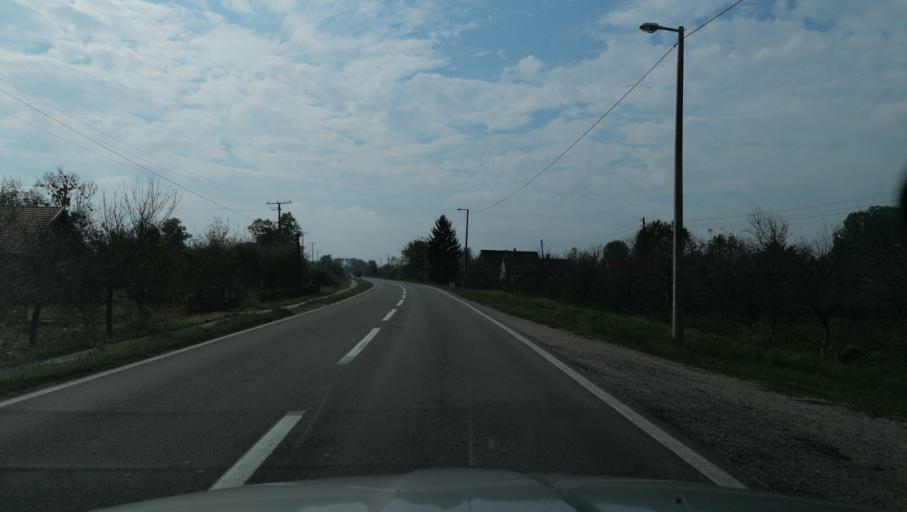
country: BA
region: Republika Srpska
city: Balatun
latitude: 44.8567
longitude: 19.3202
